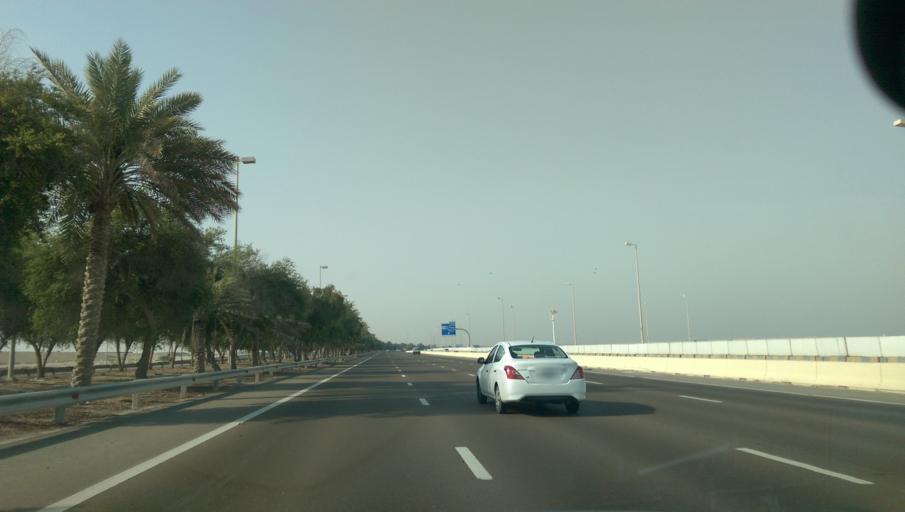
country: AE
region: Abu Dhabi
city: Abu Dhabi
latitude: 24.4260
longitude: 54.6774
